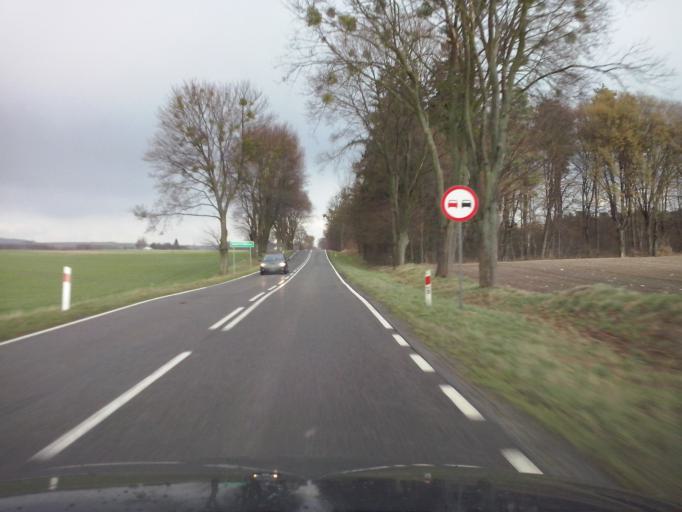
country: PL
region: Lublin Voivodeship
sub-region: Powiat krasnostawski
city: Krasnystaw
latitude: 51.0216
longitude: 23.2048
